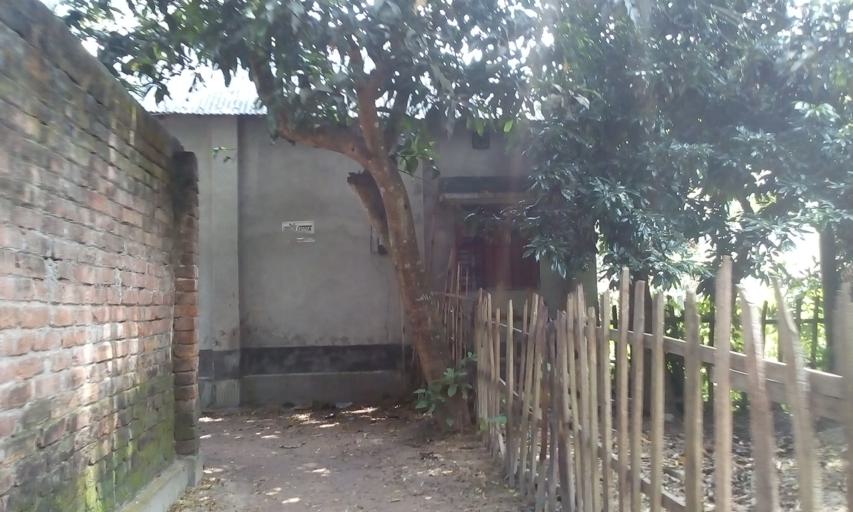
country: IN
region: West Bengal
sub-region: Dakshin Dinajpur
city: Balurghat
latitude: 25.3808
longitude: 88.9882
